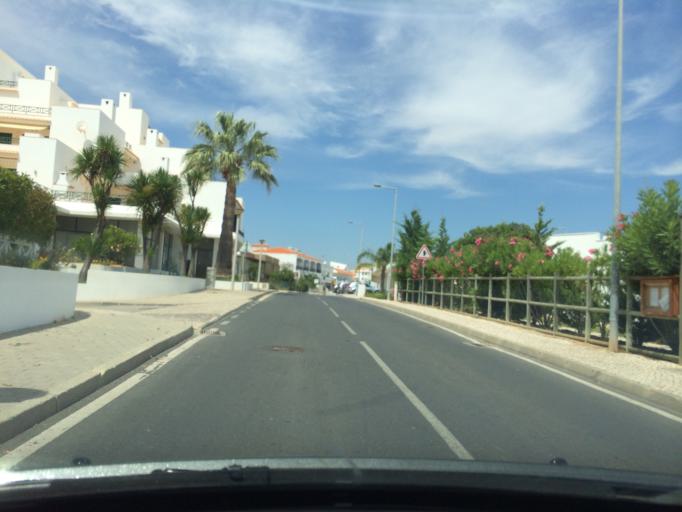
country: PT
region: Faro
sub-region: Albufeira
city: Albufeira
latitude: 37.0902
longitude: -8.1958
